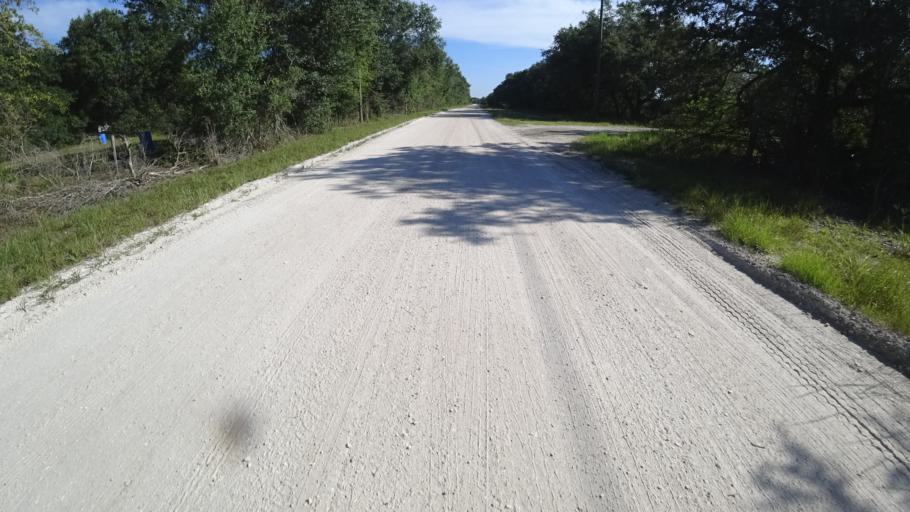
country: US
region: Florida
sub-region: Sarasota County
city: Lake Sarasota
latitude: 27.4121
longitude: -82.2520
